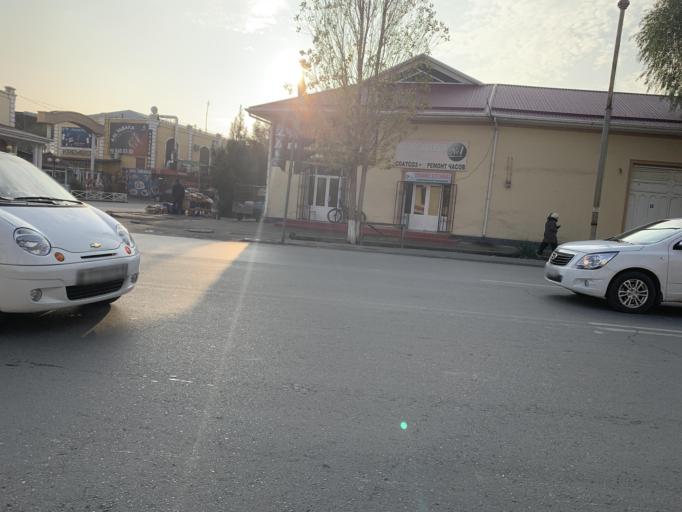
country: UZ
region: Fergana
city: Qo`qon
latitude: 40.5381
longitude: 70.9252
